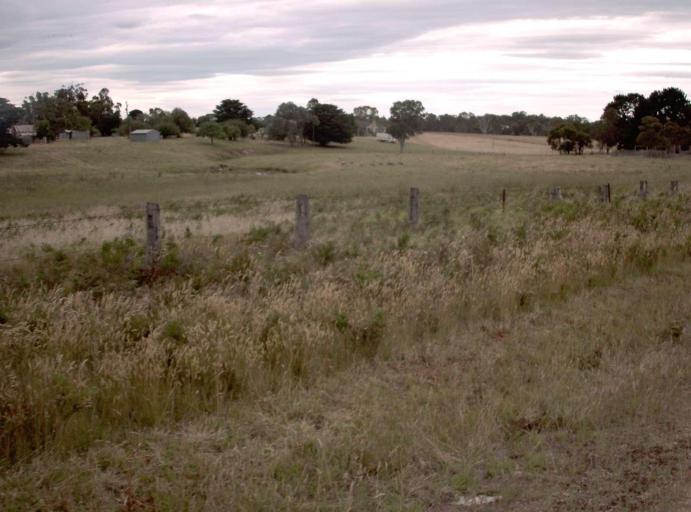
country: AU
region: Victoria
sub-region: East Gippsland
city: Bairnsdale
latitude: -37.9787
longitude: 147.4597
